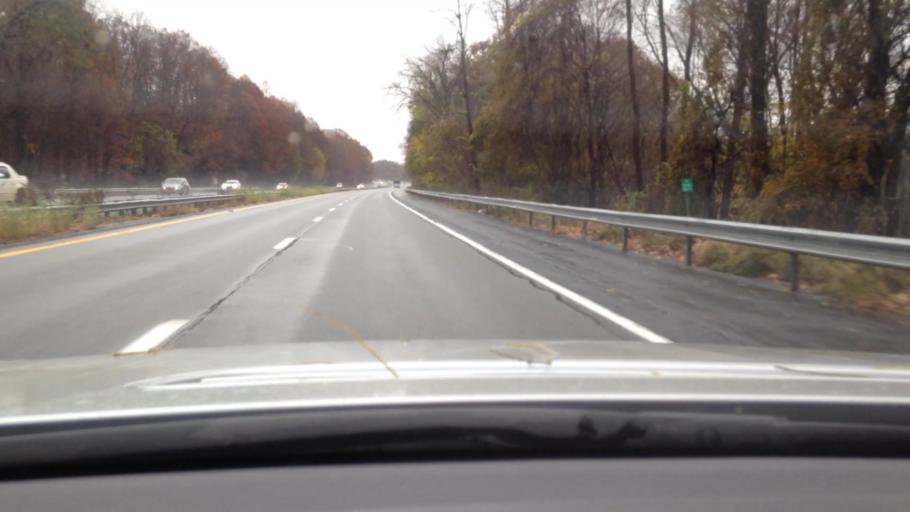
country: US
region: New York
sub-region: Westchester County
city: Buchanan
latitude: 41.2611
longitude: -73.9314
